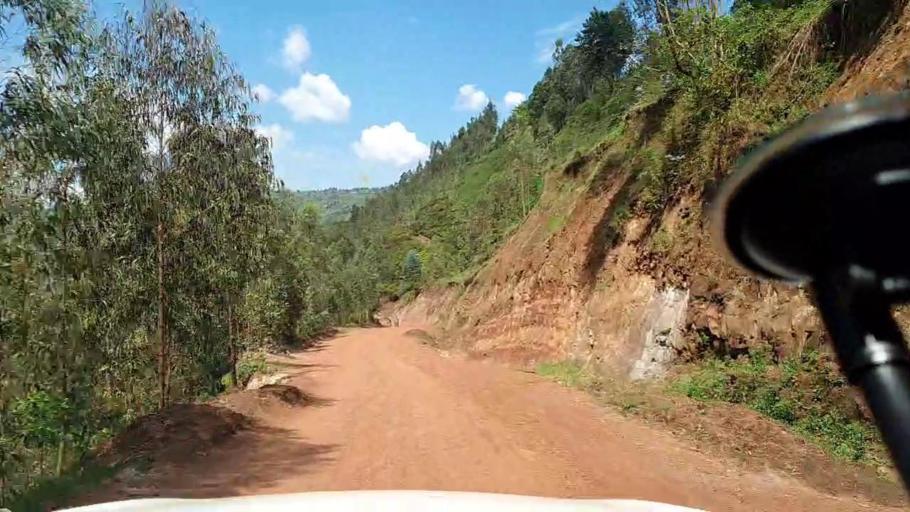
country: RW
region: Kigali
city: Kigali
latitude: -1.8006
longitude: 29.8928
